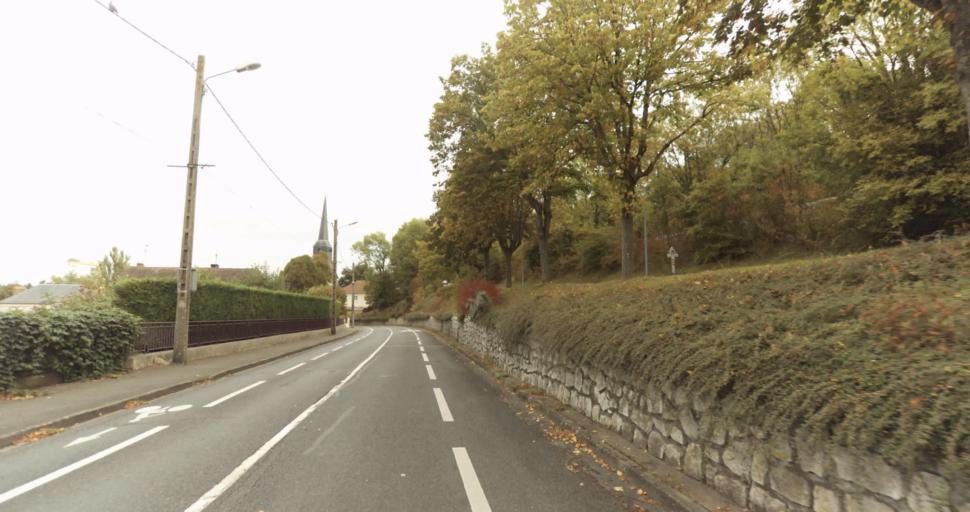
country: FR
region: Centre
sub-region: Departement d'Eure-et-Loir
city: Vernouillet
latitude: 48.7189
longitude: 1.3566
